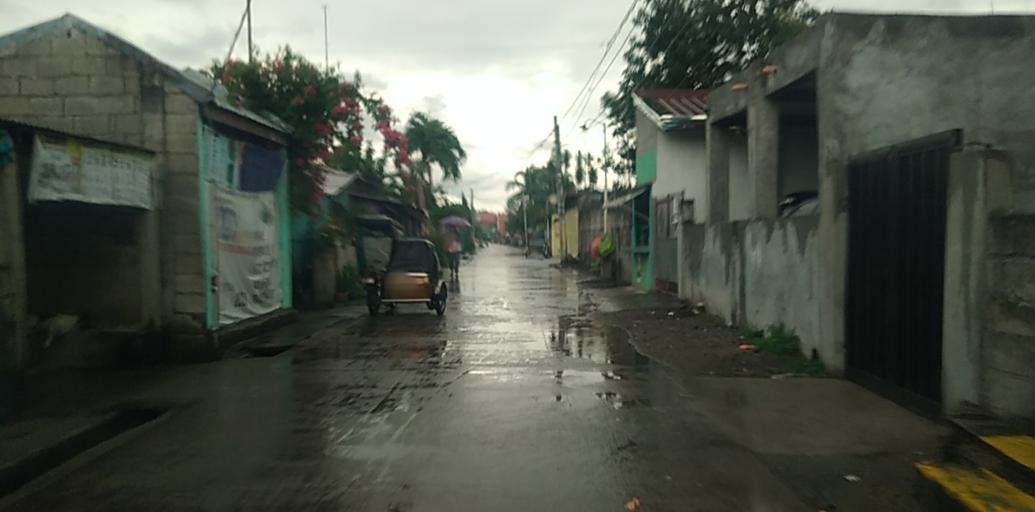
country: PH
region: Central Luzon
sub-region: Province of Pampanga
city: Anao
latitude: 15.1552
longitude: 120.7232
